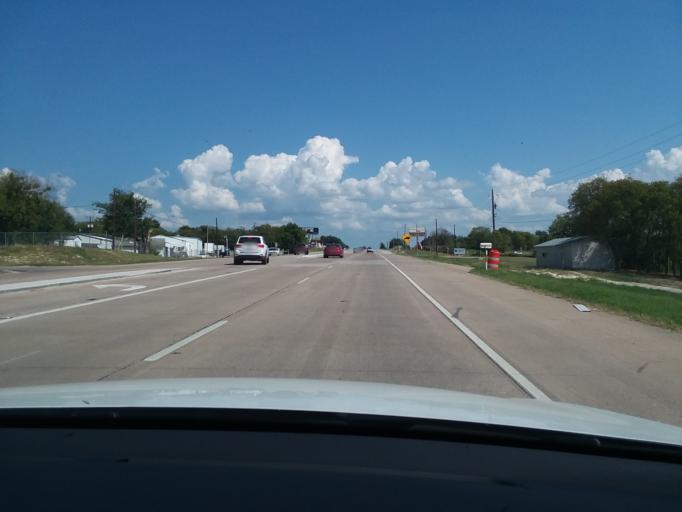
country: US
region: Texas
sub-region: Collin County
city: McKinney
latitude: 33.1980
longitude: -96.5749
